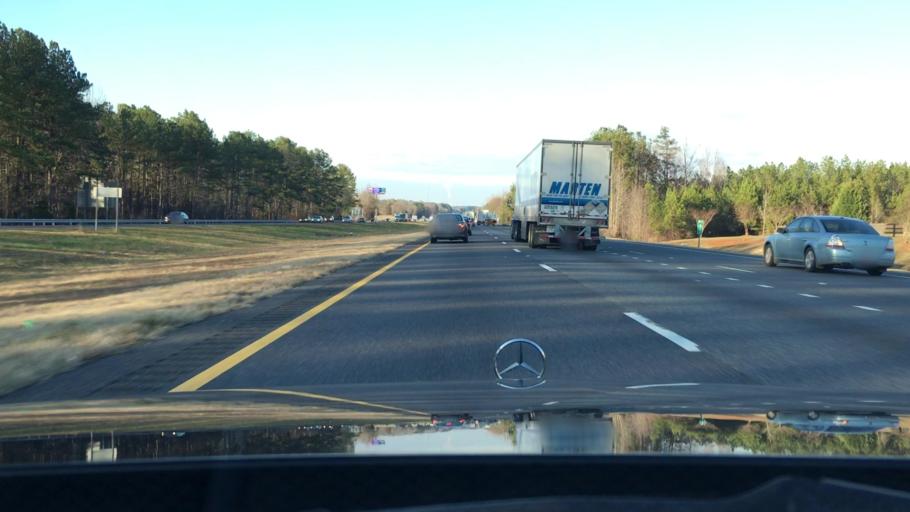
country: US
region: South Carolina
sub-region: Chester County
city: Eureka Mill
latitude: 34.7500
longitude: -81.0357
